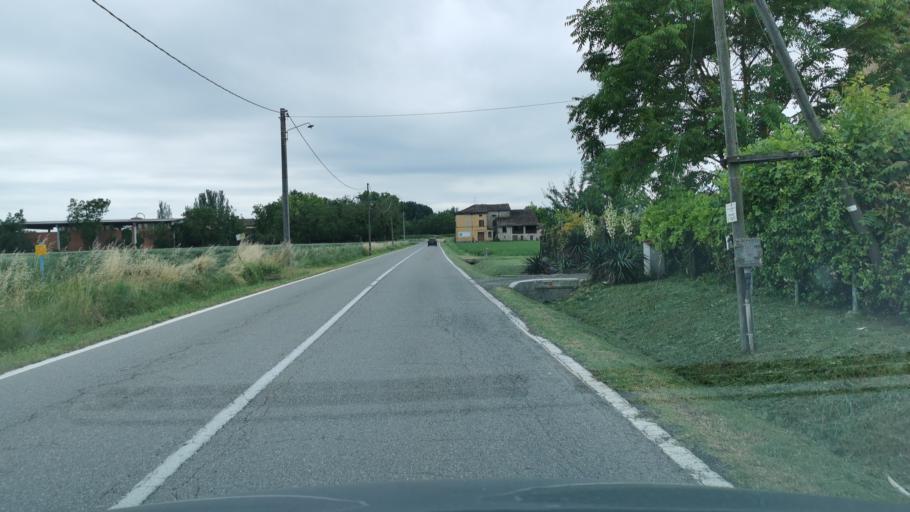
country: IT
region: Emilia-Romagna
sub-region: Provincia di Parma
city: Soragna
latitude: 44.9002
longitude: 10.0923
